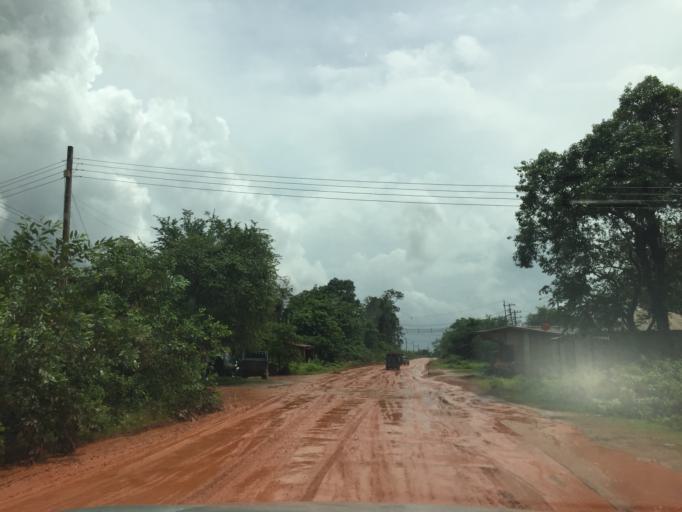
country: LA
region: Attapu
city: Attapu
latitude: 14.8143
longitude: 106.7861
